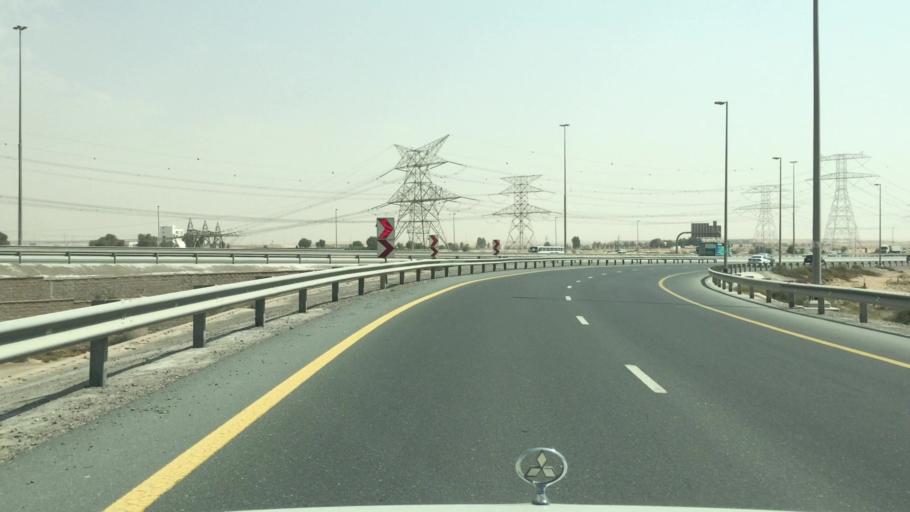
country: AE
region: Dubai
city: Dubai
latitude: 25.0866
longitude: 55.3894
